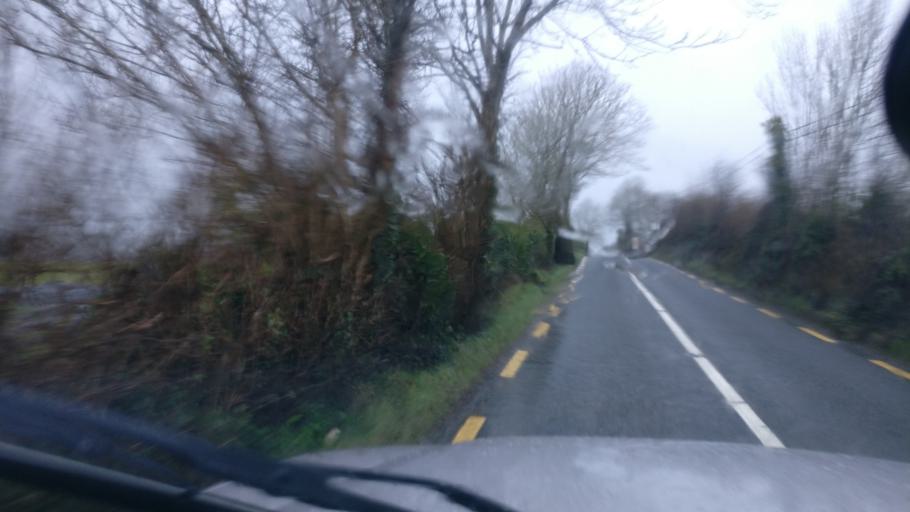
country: IE
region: Connaught
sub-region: County Galway
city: Loughrea
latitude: 53.1570
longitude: -8.4827
